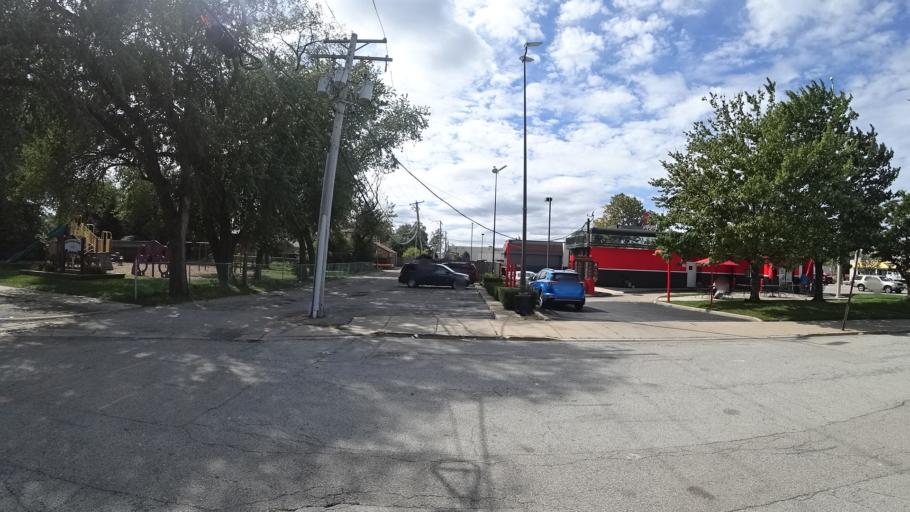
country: US
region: Illinois
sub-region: Cook County
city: Oak Lawn
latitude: 41.7193
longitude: -87.7713
